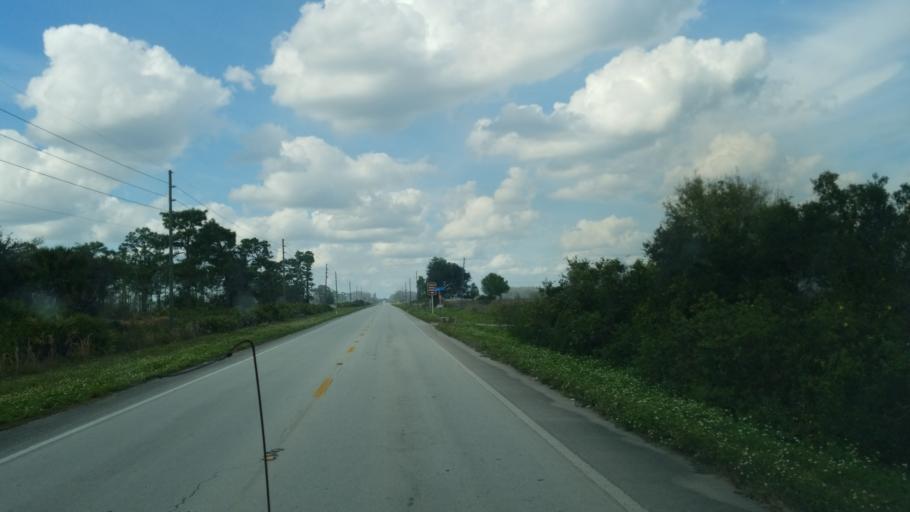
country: US
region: Florida
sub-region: Osceola County
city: Saint Cloud
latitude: 28.0544
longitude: -81.0560
